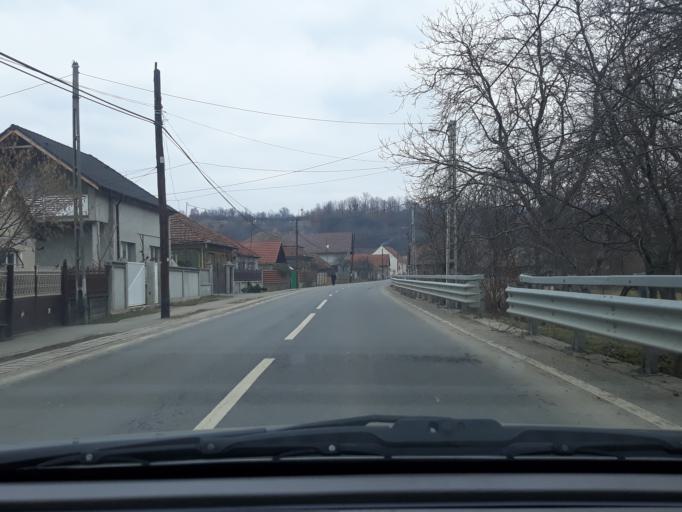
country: RO
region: Bihor
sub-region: Oras Alesd
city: Pestis
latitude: 47.0696
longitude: 22.4089
